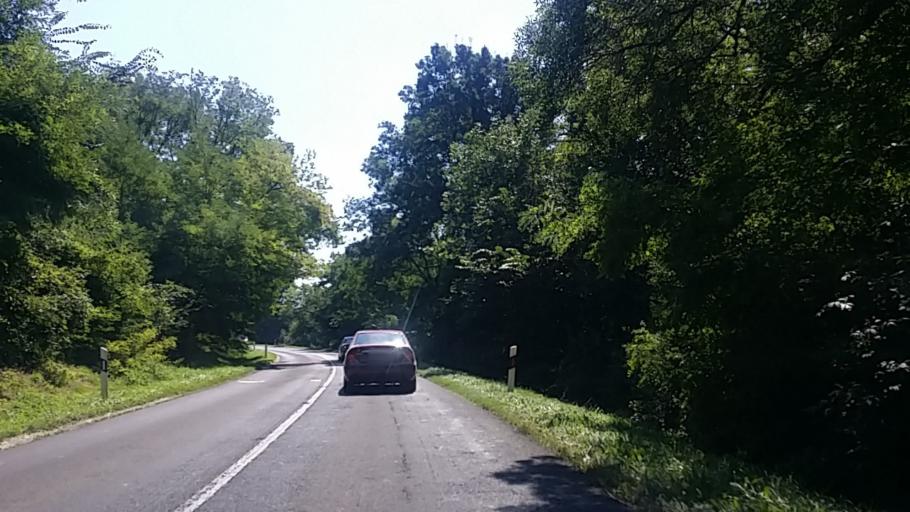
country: HU
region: Zala
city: Keszthely
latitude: 46.7041
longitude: 17.2391
